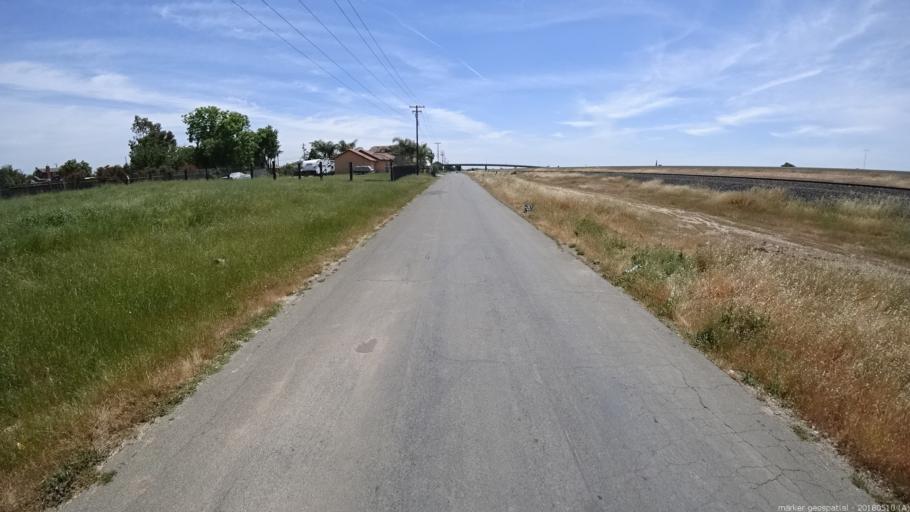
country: US
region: California
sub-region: Sacramento County
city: Sacramento
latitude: 38.6345
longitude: -121.4700
